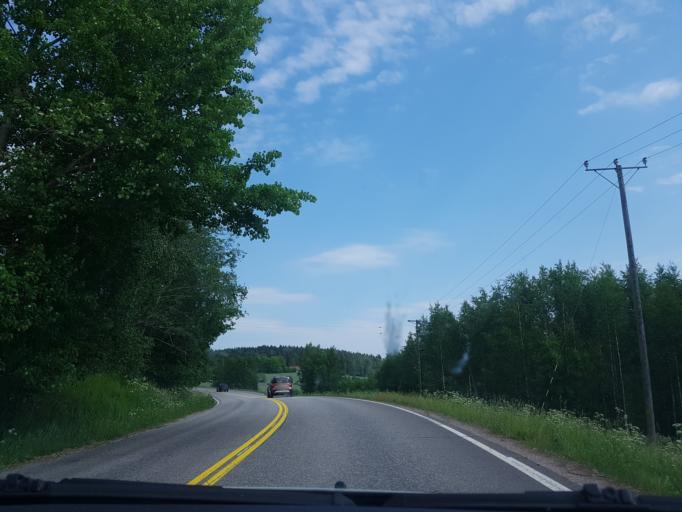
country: FI
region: Uusimaa
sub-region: Helsinki
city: Vihti
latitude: 60.3139
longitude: 24.4041
